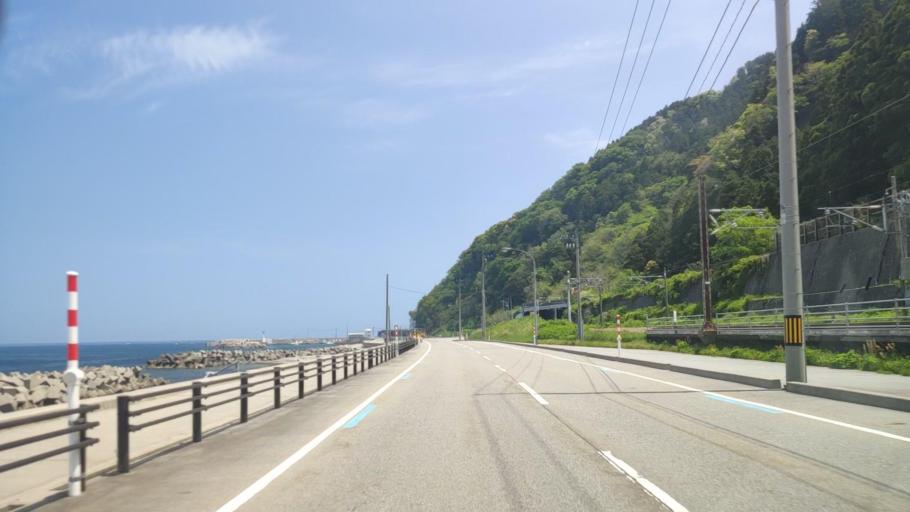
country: JP
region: Toyama
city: Nyuzen
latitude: 36.9687
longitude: 137.5814
